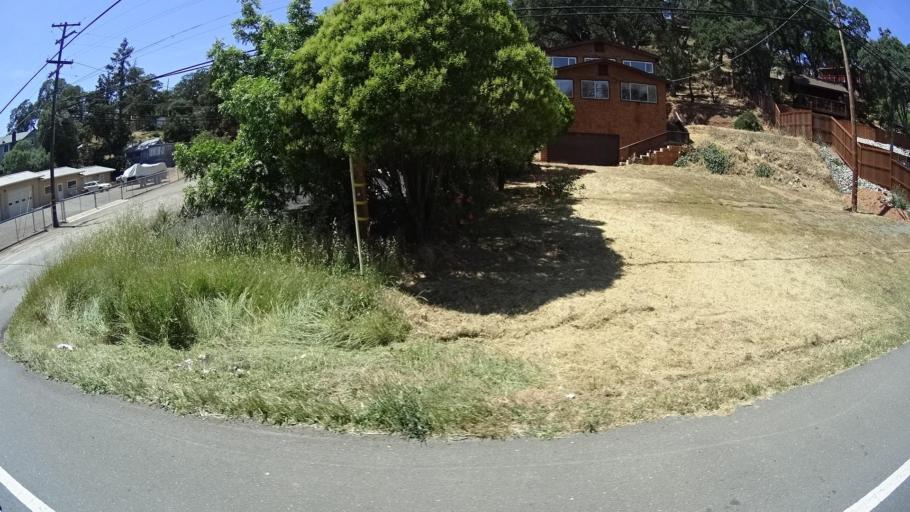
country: US
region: California
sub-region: Lake County
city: Clearlake Oaks
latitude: 39.0210
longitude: -122.6757
